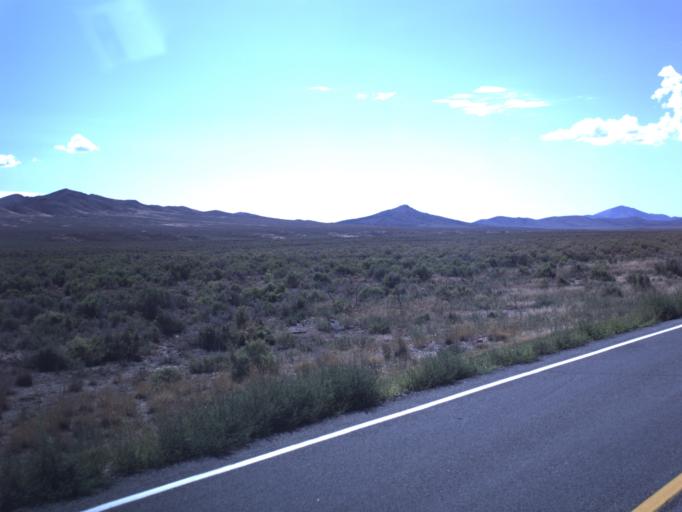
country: US
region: Utah
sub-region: Tooele County
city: Tooele
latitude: 40.1565
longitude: -112.4308
